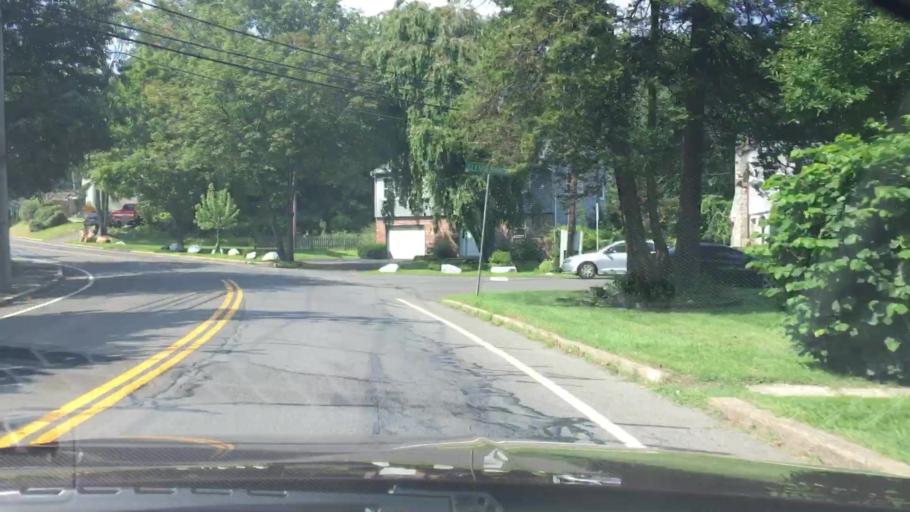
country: US
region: Connecticut
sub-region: Fairfield County
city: Norwalk
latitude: 41.1264
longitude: -73.4106
